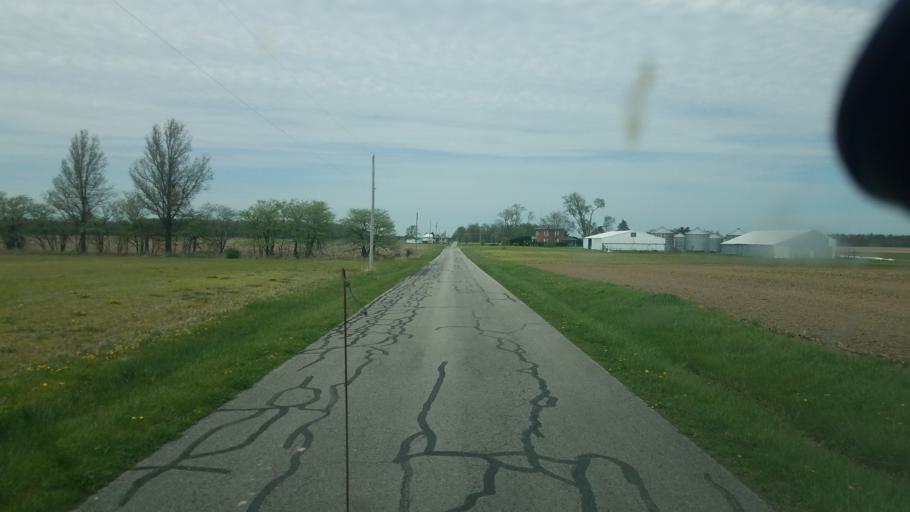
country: US
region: Ohio
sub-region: Hardin County
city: Ada
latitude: 40.8438
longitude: -83.7470
